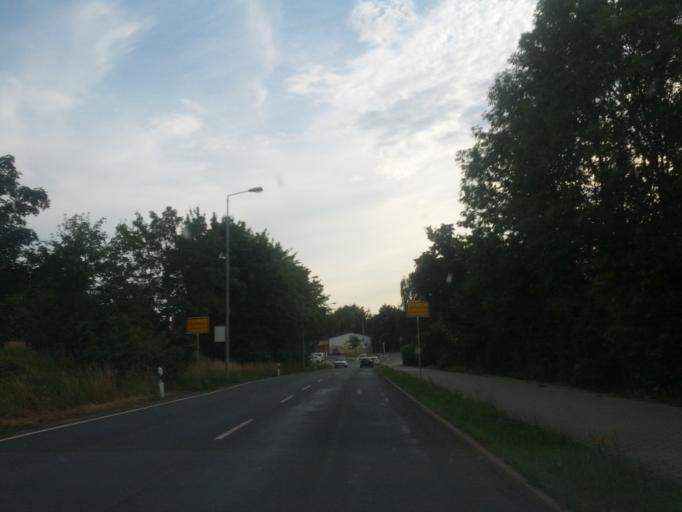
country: DE
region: Thuringia
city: Ingersleben
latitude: 50.9555
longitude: 10.9749
